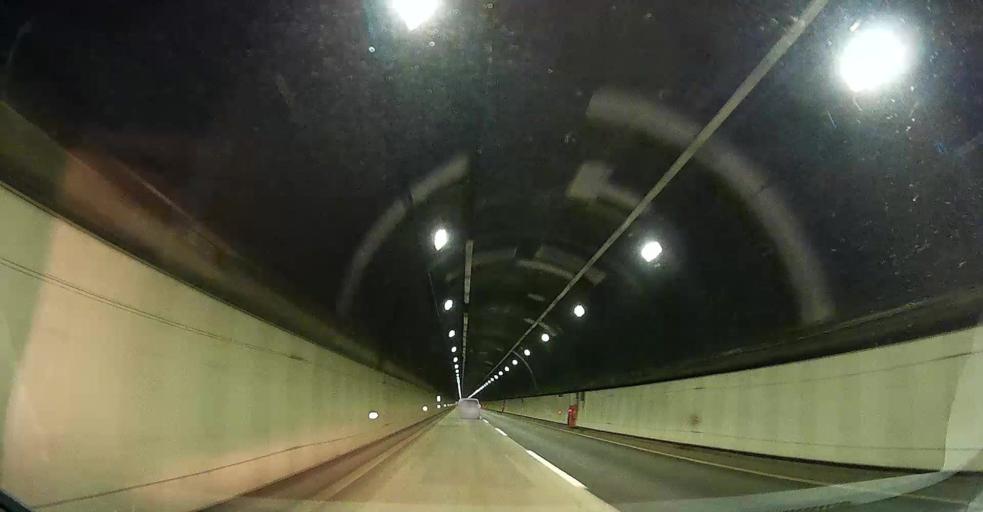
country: JP
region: Kanagawa
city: Ninomiya
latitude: 35.2937
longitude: 139.2073
